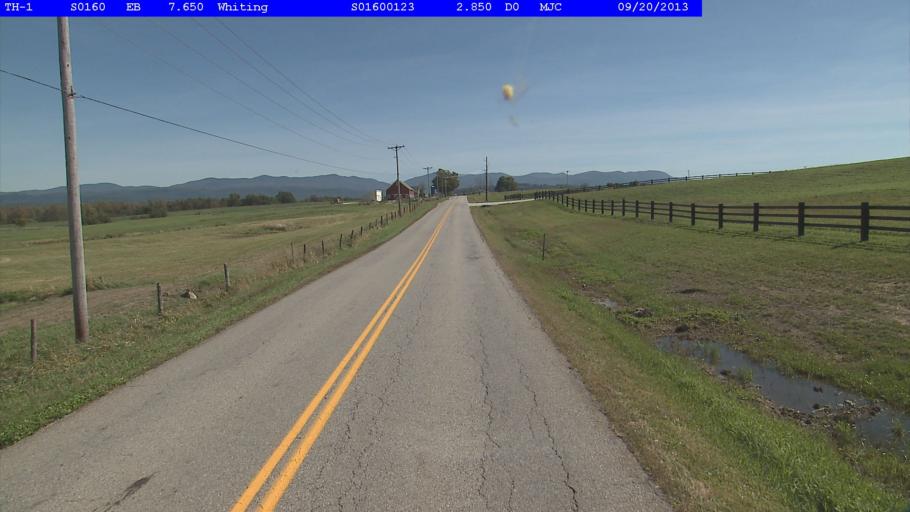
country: US
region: Vermont
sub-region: Rutland County
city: Brandon
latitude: 43.8531
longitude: -73.1737
